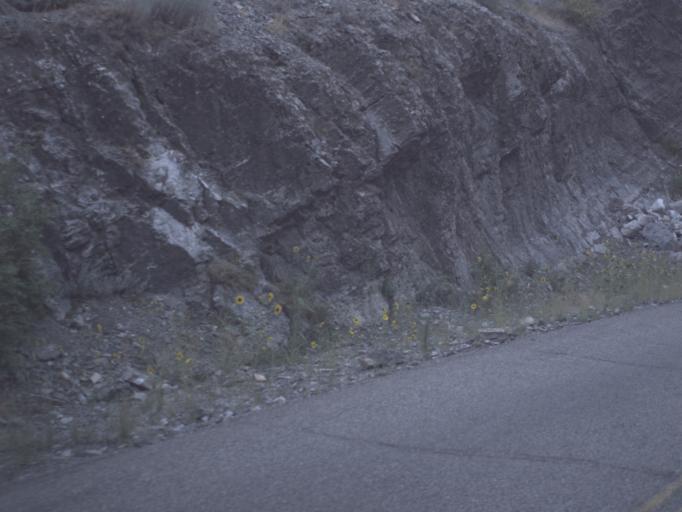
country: US
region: Utah
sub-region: Utah County
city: Orem
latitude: 40.3748
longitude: -111.5684
